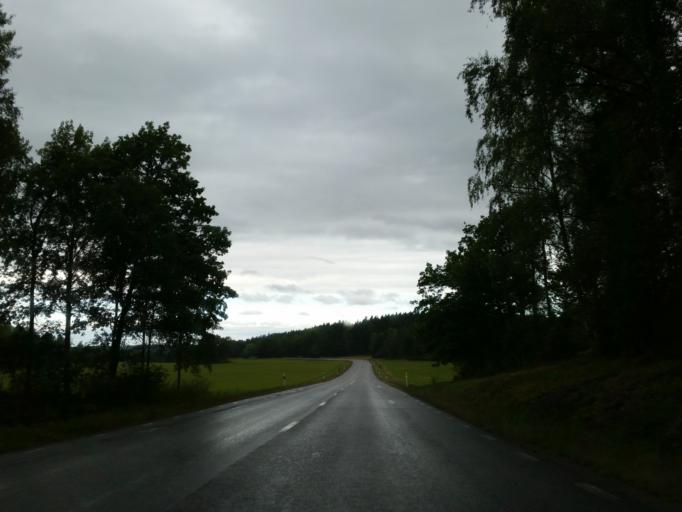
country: SE
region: Uppsala
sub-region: Habo Kommun
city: Balsta
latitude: 59.6471
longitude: 17.4283
